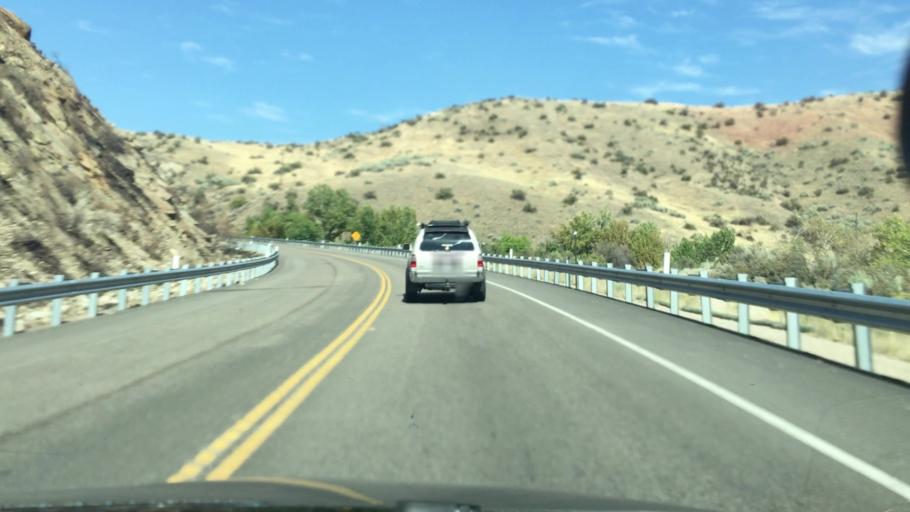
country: US
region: Idaho
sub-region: Ada County
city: Eagle
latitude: 43.7606
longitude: -116.2691
